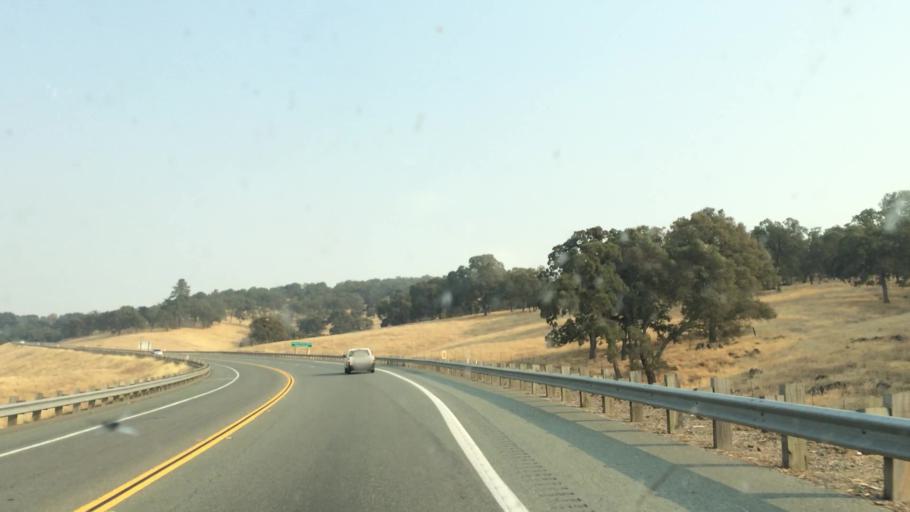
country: US
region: California
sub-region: Amador County
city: Sutter Creek
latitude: 38.4170
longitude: -120.8407
